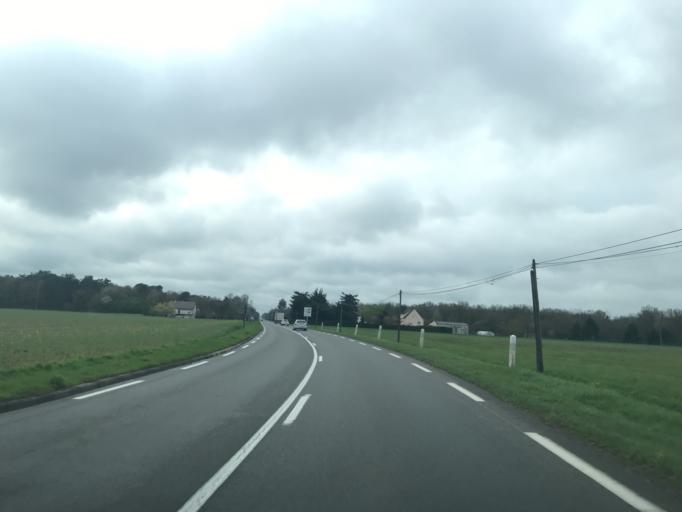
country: FR
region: Centre
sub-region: Departement du Loiret
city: Bray-en-Val
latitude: 47.8334
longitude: 2.3639
